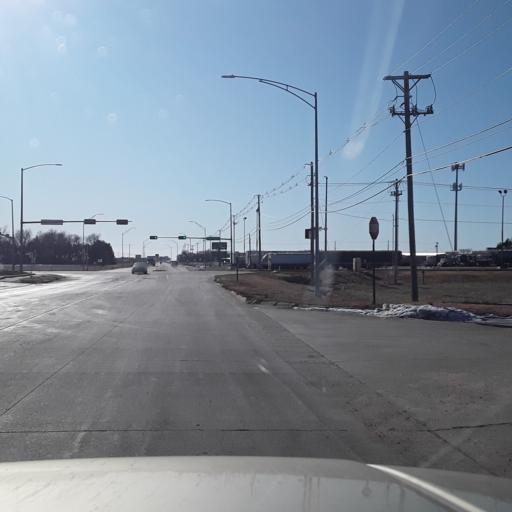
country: US
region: Nebraska
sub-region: Adams County
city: Hastings
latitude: 40.5691
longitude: -98.4021
